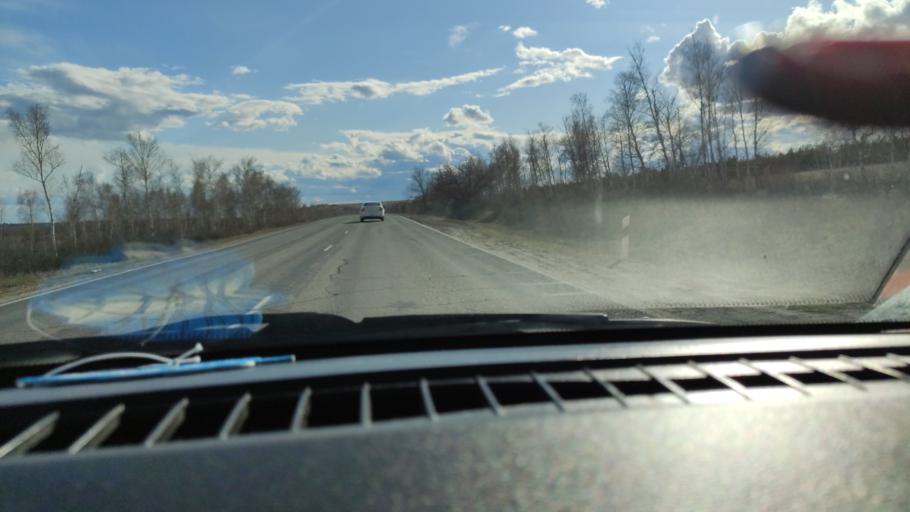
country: RU
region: Saratov
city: Sennoy
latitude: 52.1092
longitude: 46.8270
